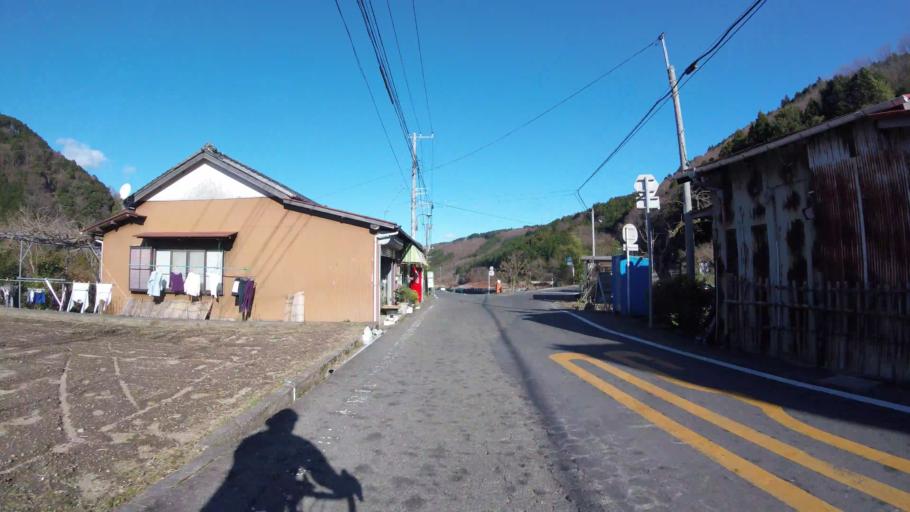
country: JP
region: Shizuoka
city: Ito
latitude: 34.9192
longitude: 138.9844
